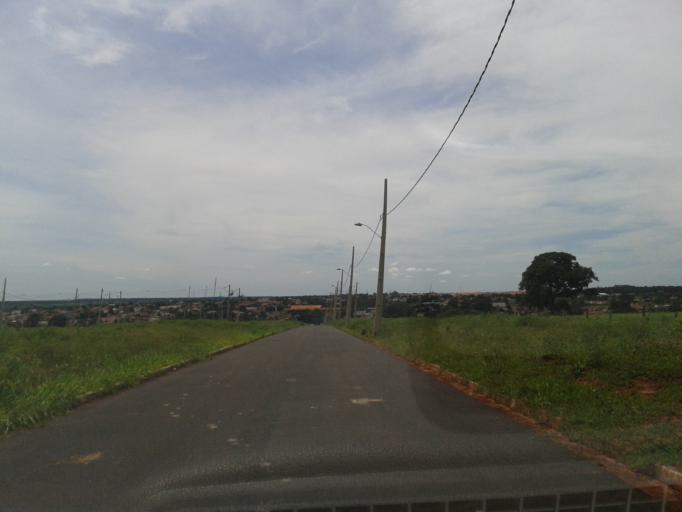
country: BR
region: Minas Gerais
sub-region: Santa Vitoria
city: Santa Vitoria
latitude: -18.8375
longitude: -50.1402
